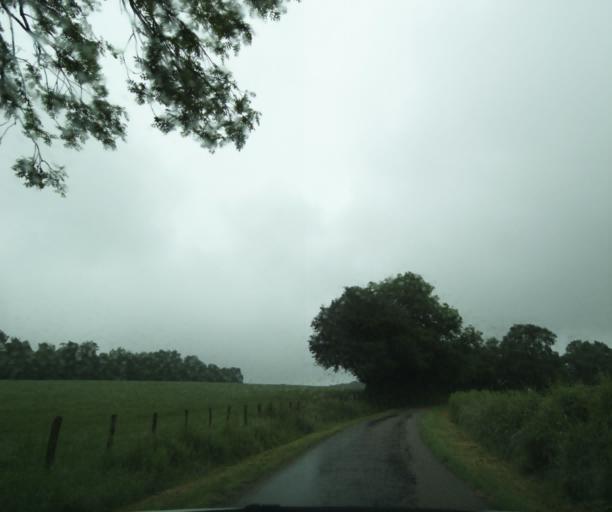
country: FR
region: Bourgogne
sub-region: Departement de Saone-et-Loire
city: Charolles
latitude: 46.4485
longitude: 4.2105
